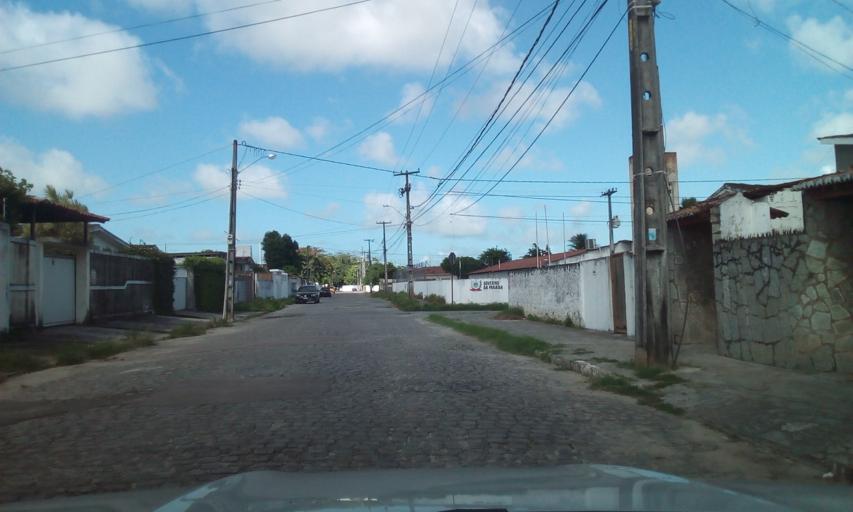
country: BR
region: Paraiba
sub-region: Joao Pessoa
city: Joao Pessoa
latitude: -7.1375
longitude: -34.8755
